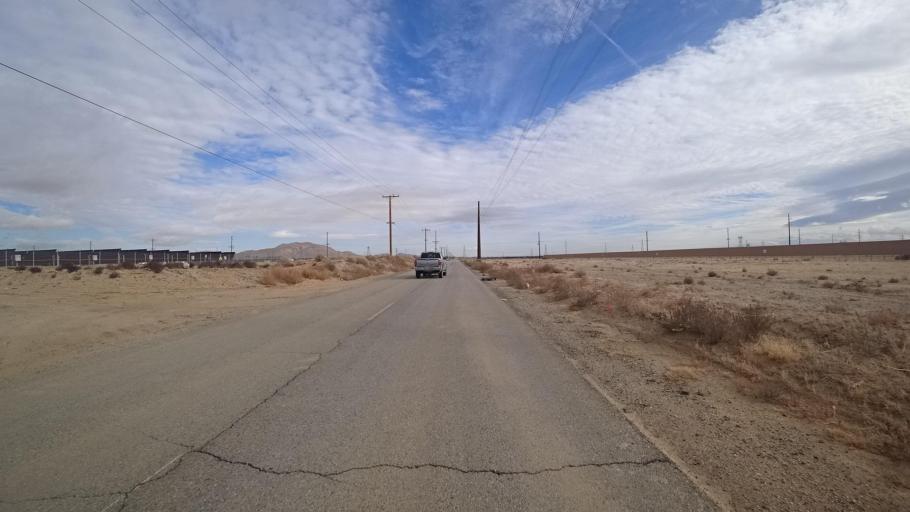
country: US
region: California
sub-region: Kern County
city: Rosamond
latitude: 34.8633
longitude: -118.3288
